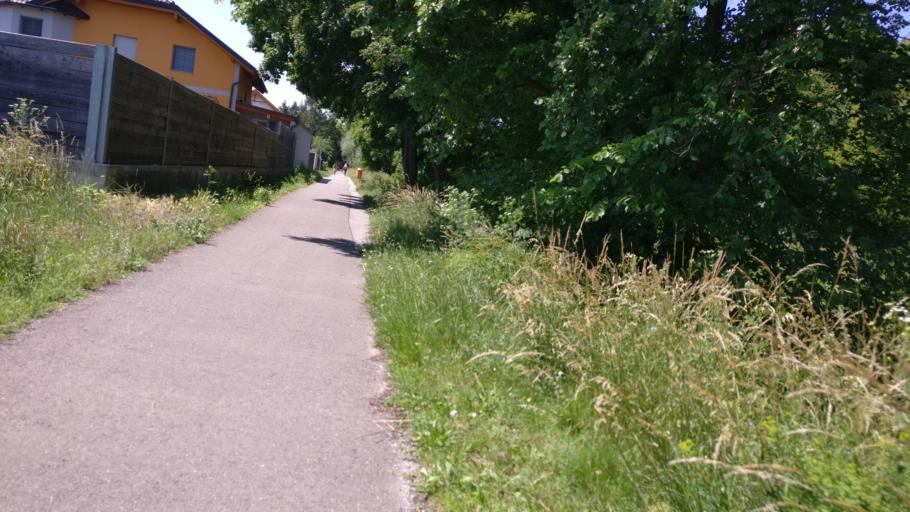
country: AT
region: Lower Austria
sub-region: Politischer Bezirk Baden
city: Oberwaltersdorf
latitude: 47.9845
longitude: 16.3322
